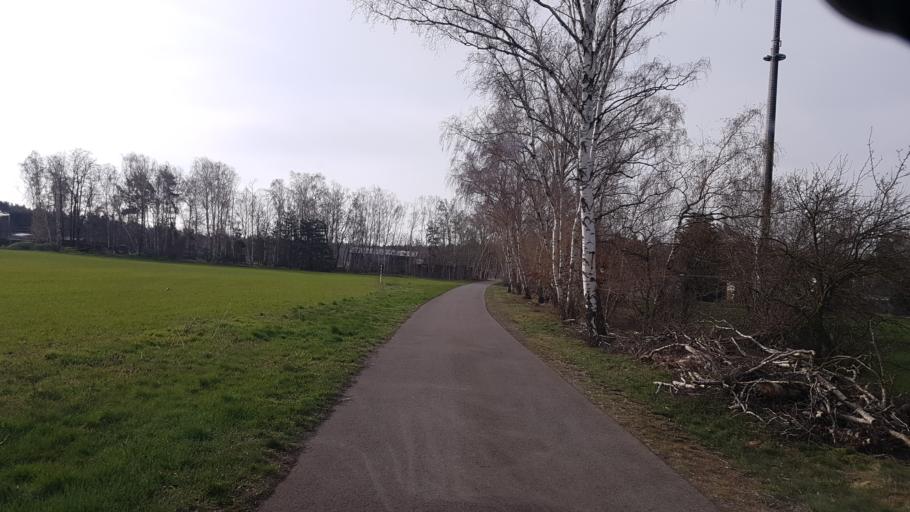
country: DE
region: Brandenburg
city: Bronkow
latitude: 51.7076
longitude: 13.8879
